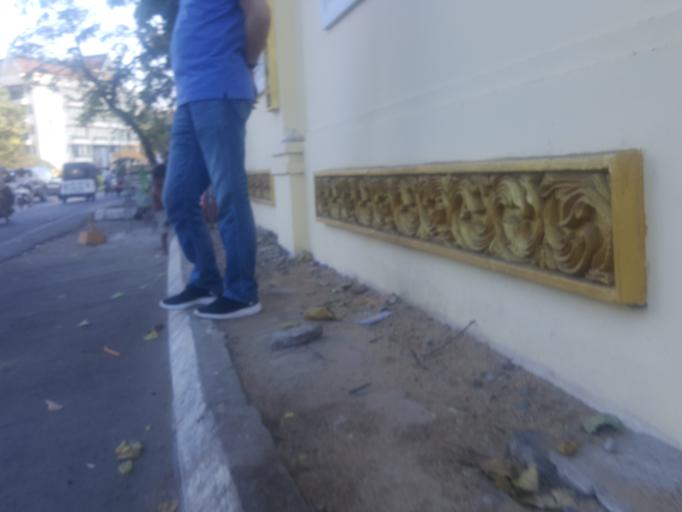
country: KH
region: Phnom Penh
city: Phnom Penh
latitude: 11.5620
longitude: 104.9348
